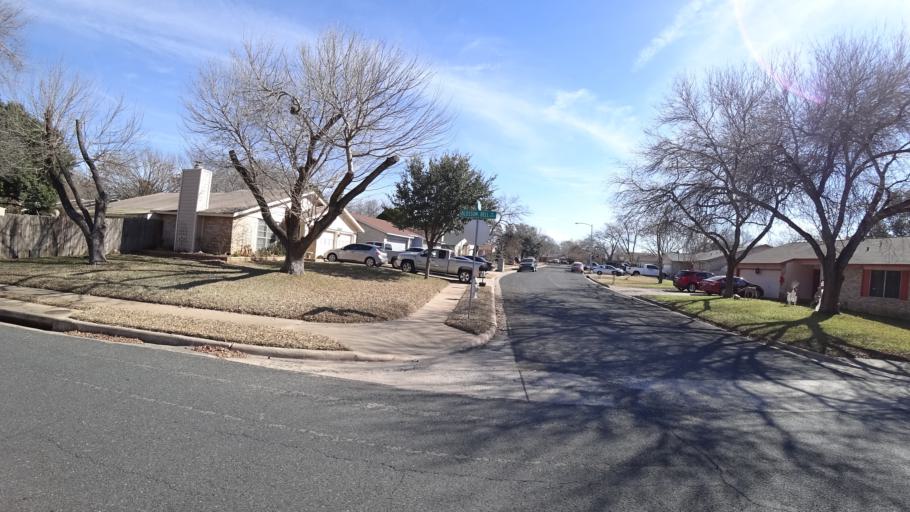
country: US
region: Texas
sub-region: Travis County
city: Wells Branch
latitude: 30.3845
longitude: -97.7005
